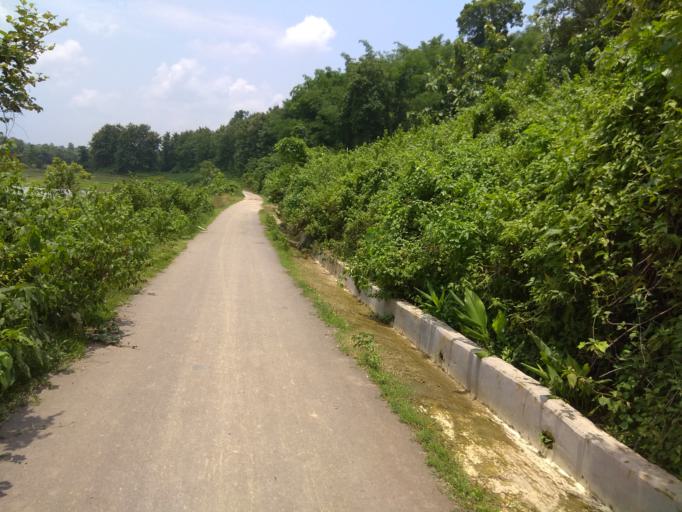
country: BD
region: Chittagong
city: Manikchari
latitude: 22.8927
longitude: 91.9216
